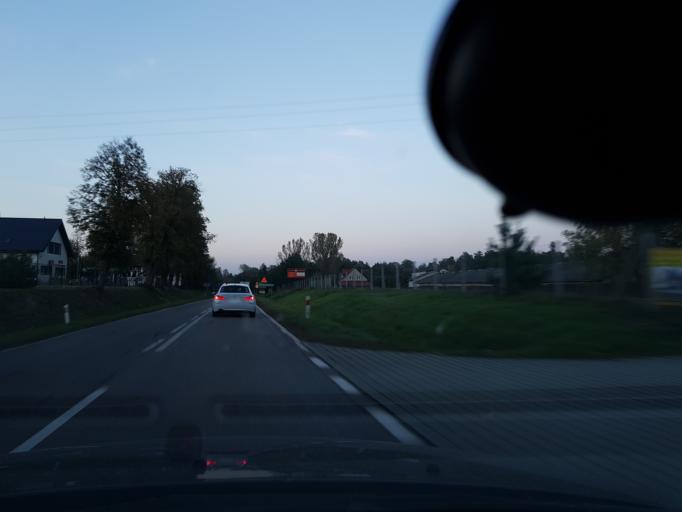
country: PL
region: Masovian Voivodeship
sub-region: Powiat zyrardowski
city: Radziejowice
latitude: 52.0420
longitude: 20.5897
